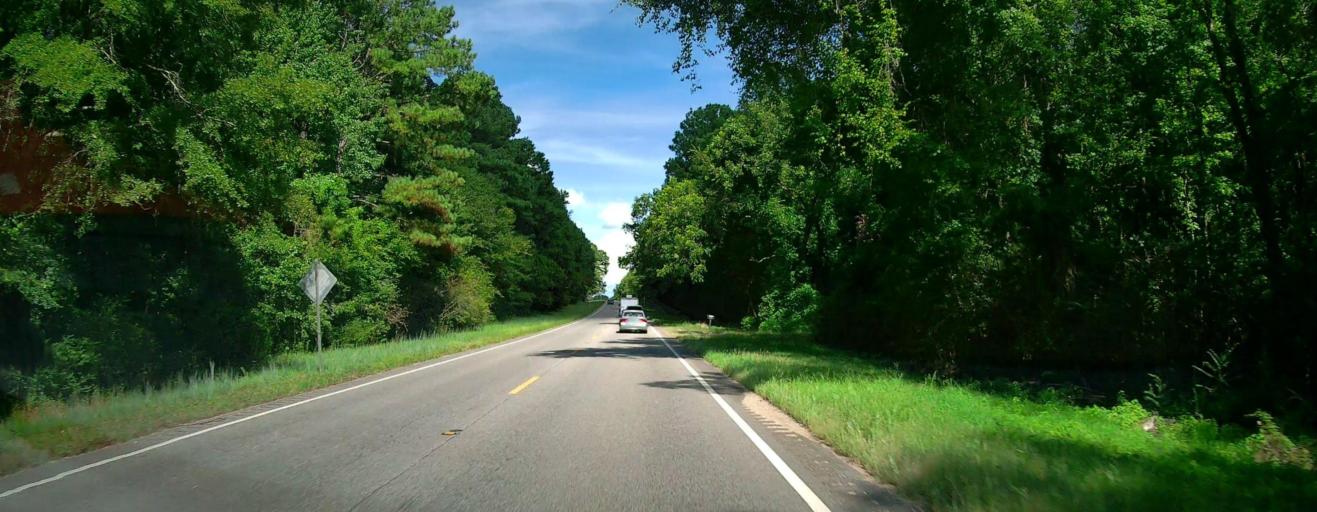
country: US
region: Alabama
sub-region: Macon County
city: Tuskegee
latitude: 32.3793
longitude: -85.7932
